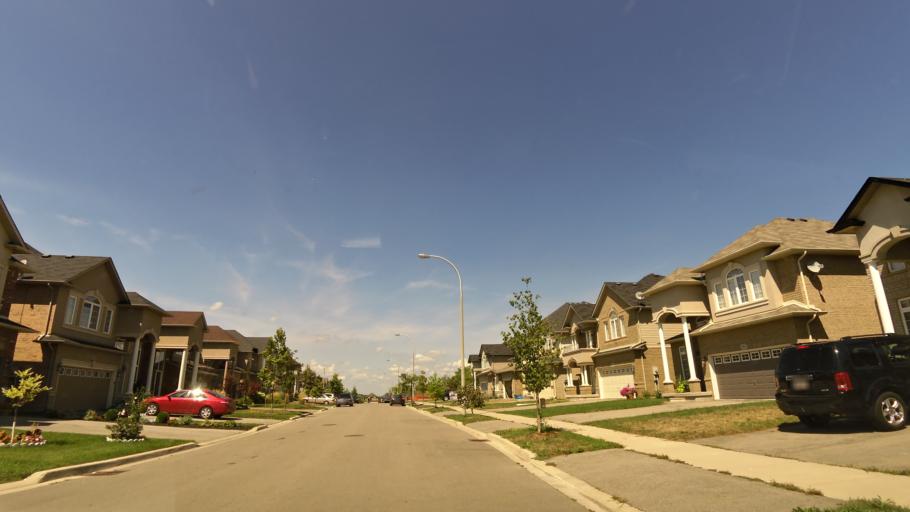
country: CA
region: Ontario
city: Ancaster
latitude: 43.2131
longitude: -79.9445
